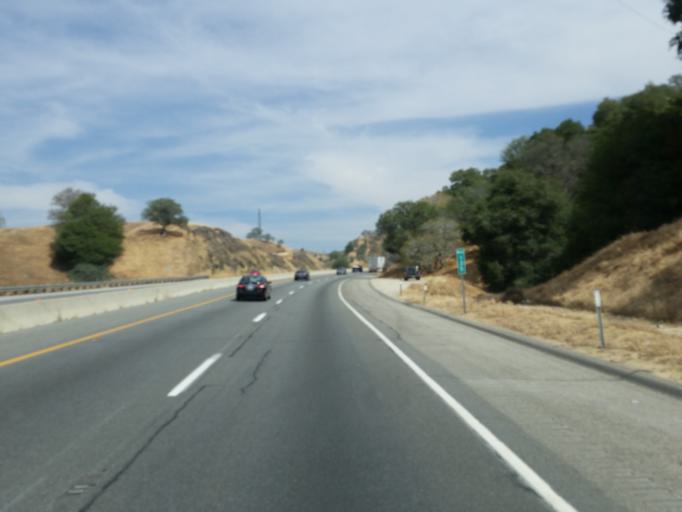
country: US
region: California
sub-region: Kern County
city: Bear Valley Springs
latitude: 35.2593
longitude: -118.6165
